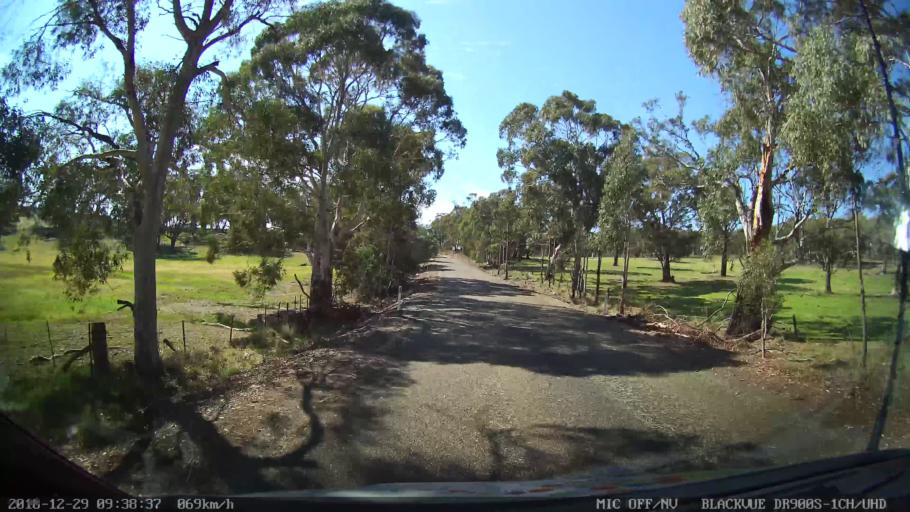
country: AU
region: New South Wales
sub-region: Upper Lachlan Shire
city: Crookwell
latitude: -34.6486
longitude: 149.3771
